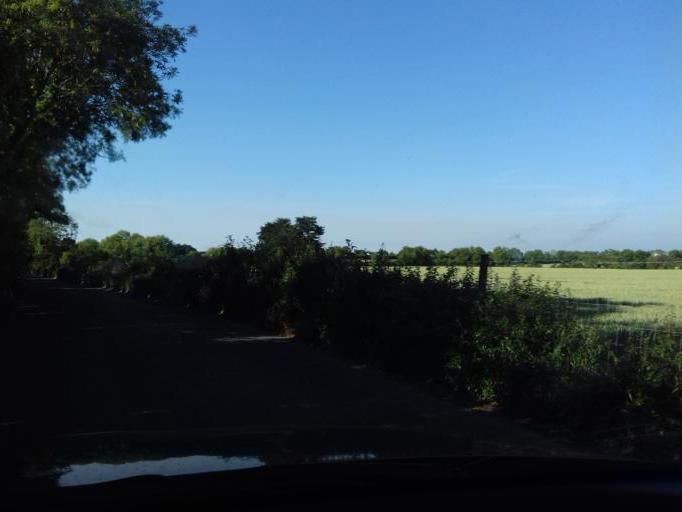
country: IE
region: Leinster
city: Ballymun
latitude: 53.4439
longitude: -6.2934
